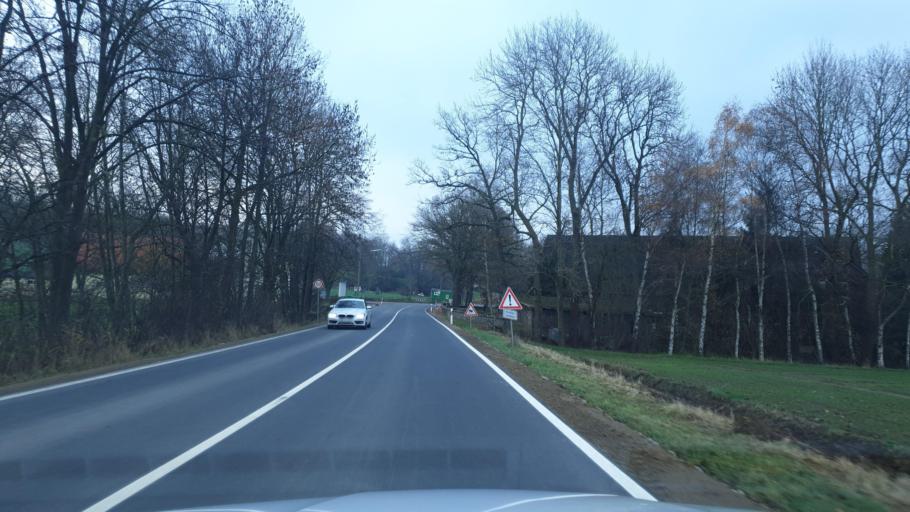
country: DE
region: North Rhine-Westphalia
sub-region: Regierungsbezirk Detmold
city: Hiddenhausen
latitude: 52.1160
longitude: 8.6223
